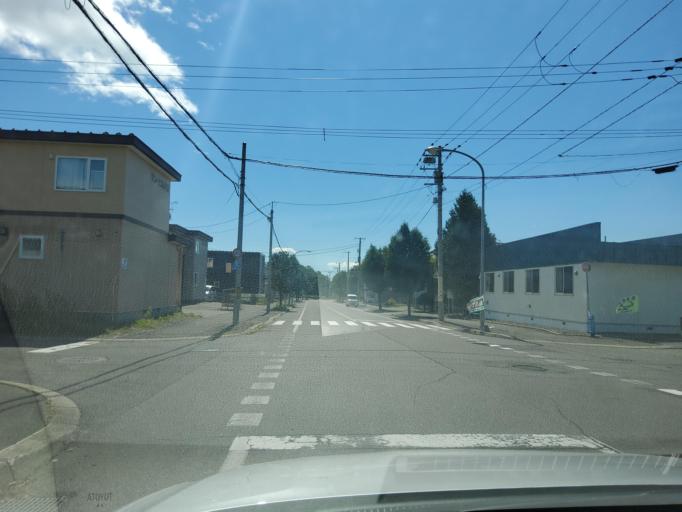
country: JP
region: Hokkaido
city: Obihiro
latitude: 42.9492
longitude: 143.1960
